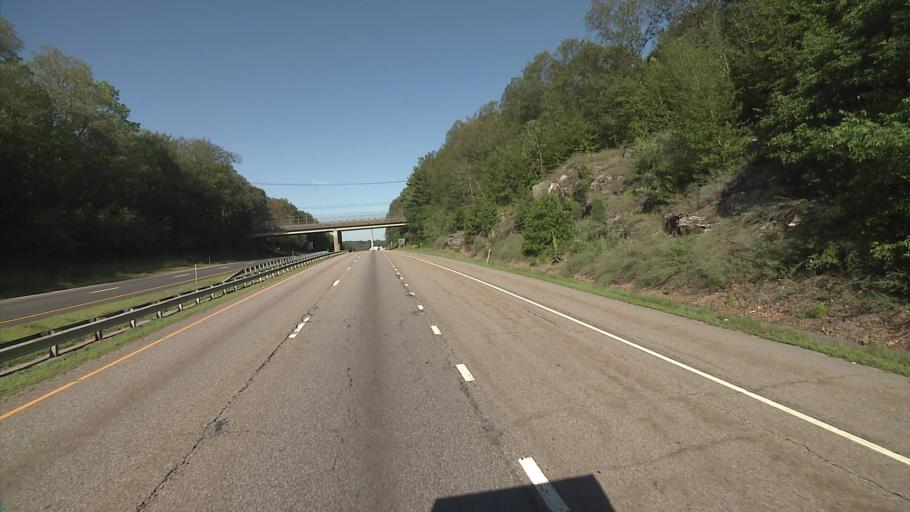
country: US
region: Connecticut
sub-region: New London County
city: Lisbon
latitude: 41.5875
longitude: -72.0290
